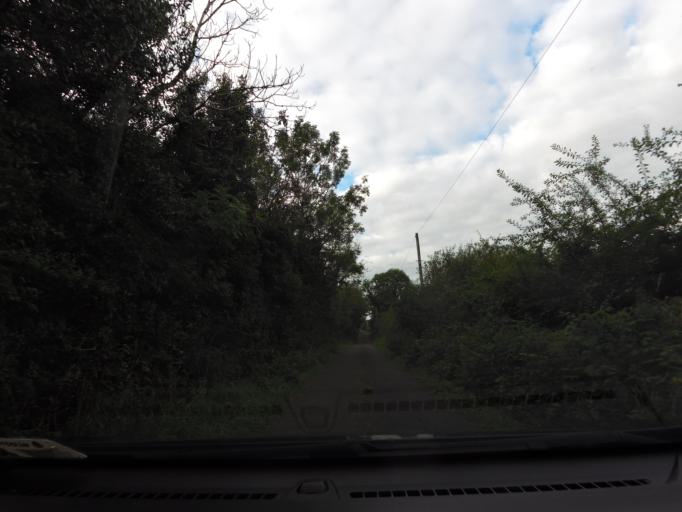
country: IE
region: Connaught
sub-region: County Galway
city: Loughrea
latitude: 53.1464
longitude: -8.5168
